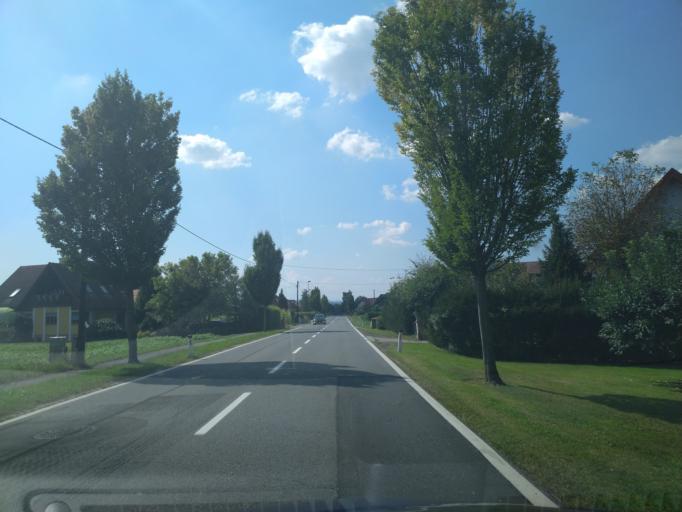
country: AT
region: Styria
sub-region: Politischer Bezirk Leibnitz
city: Obervogau
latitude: 46.7578
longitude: 15.6014
